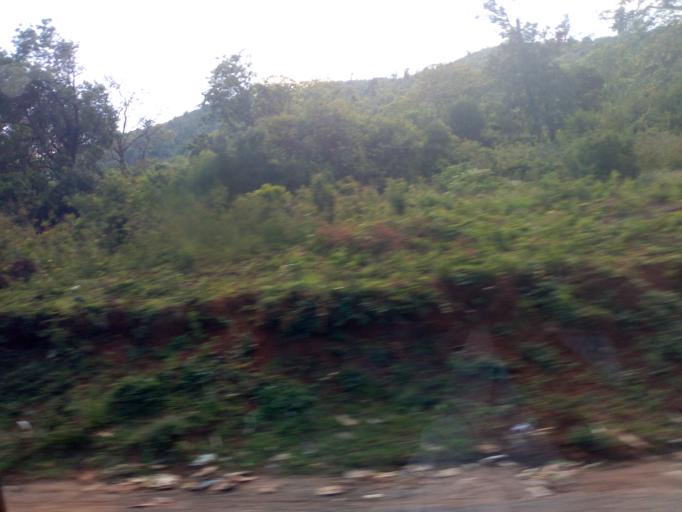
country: KE
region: Nakuru
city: Kijabe
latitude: -1.0189
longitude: 36.6026
